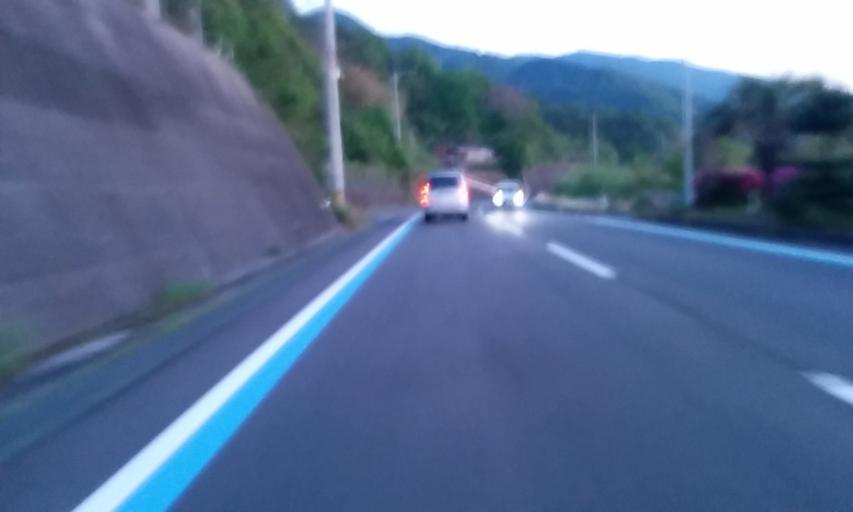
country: JP
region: Ehime
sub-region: Nishiuwa-gun
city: Ikata-cho
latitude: 33.5530
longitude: 132.4267
